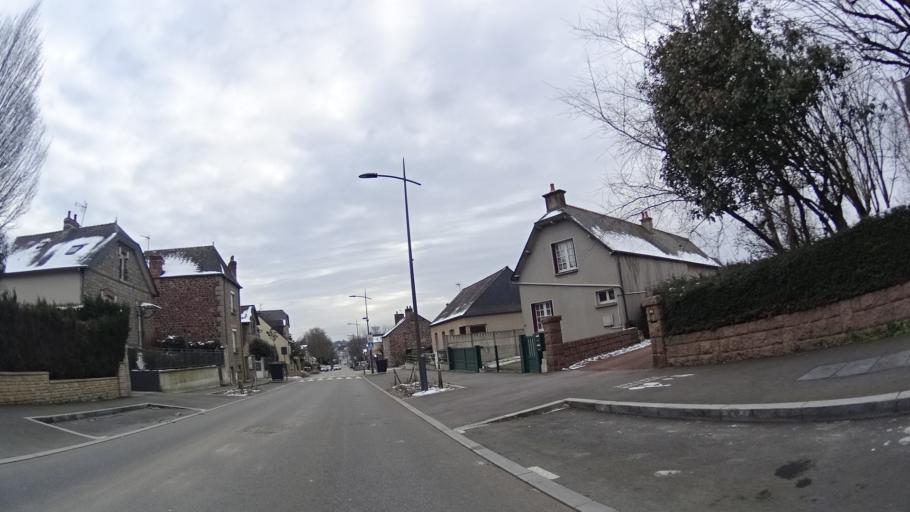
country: FR
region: Brittany
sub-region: Departement d'Ille-et-Vilaine
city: Montauban-de-Bretagne
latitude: 48.1964
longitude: -2.0488
